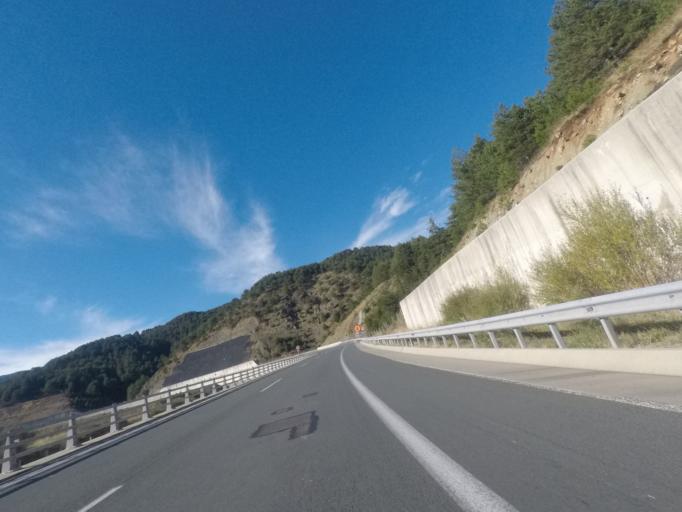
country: GR
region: Epirus
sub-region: Nomos Ioanninon
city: Metsovo
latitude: 39.7886
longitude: 21.2803
